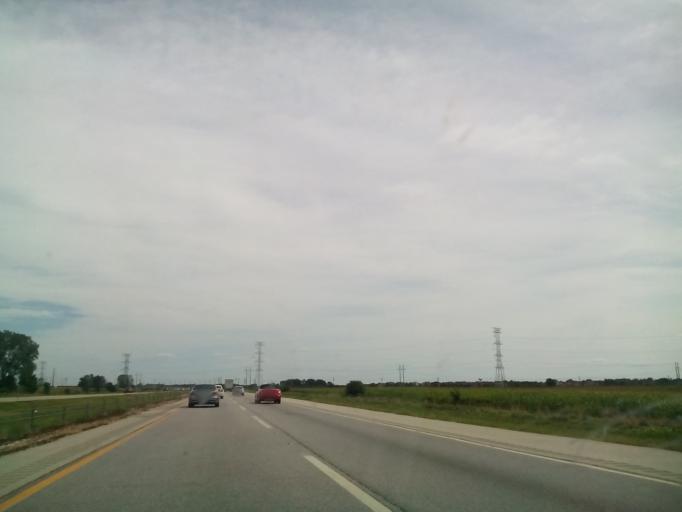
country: US
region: Illinois
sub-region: Kane County
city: Sugar Grove
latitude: 41.8089
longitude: -88.4422
